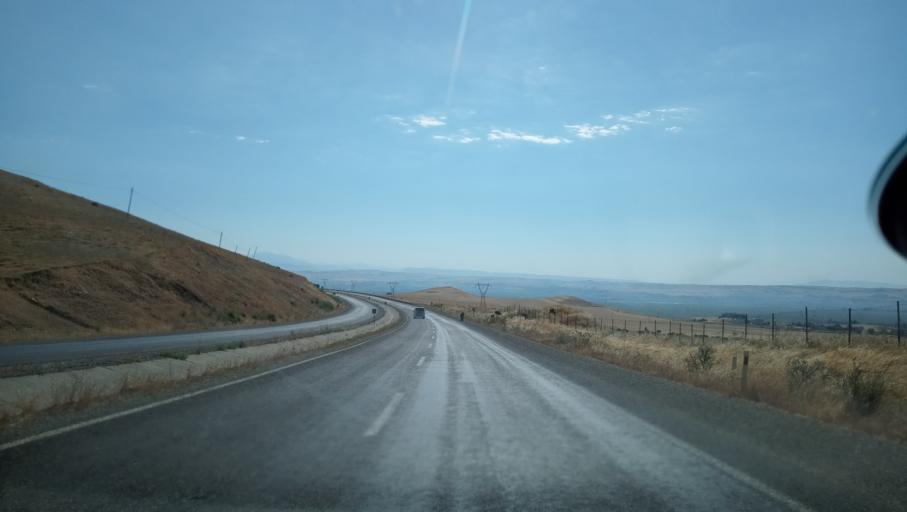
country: TR
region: Diyarbakir
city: Malabadi
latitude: 38.1180
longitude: 41.1388
